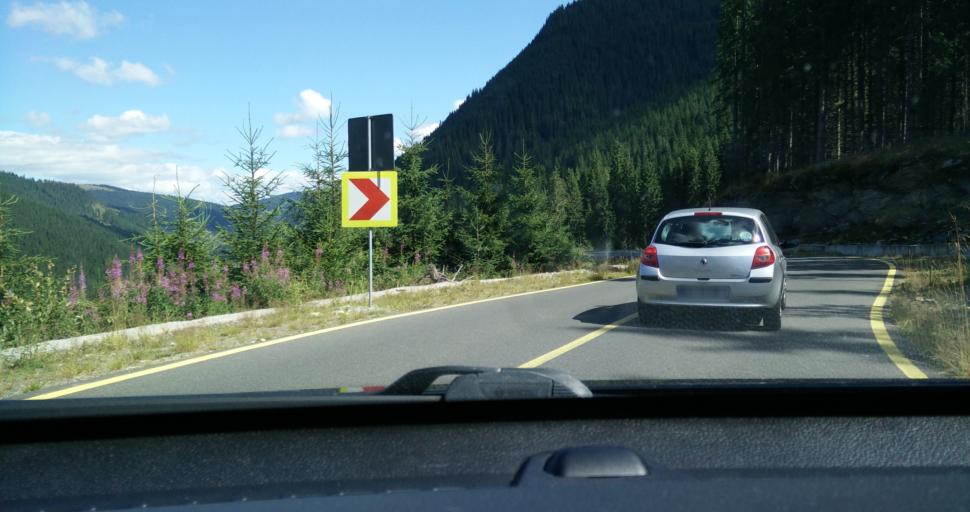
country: RO
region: Gorj
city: Novaci-Straini
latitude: 45.3933
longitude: 23.6316
